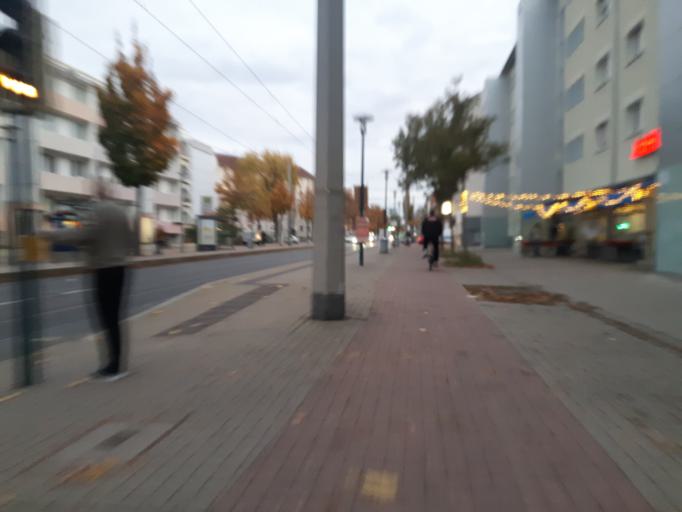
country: DE
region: Rheinland-Pfalz
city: Altrip
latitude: 49.4321
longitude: 8.5283
